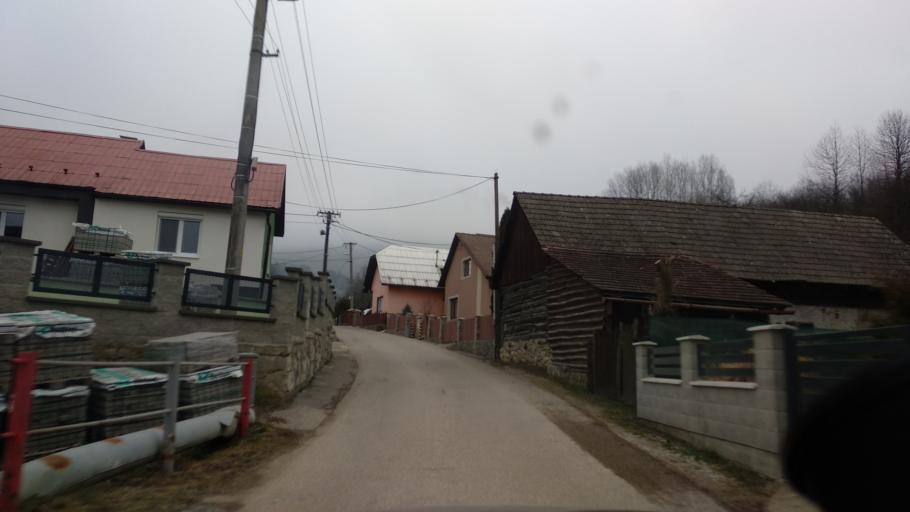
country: SK
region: Nitriansky
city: Ilava
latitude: 48.9137
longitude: 18.3006
